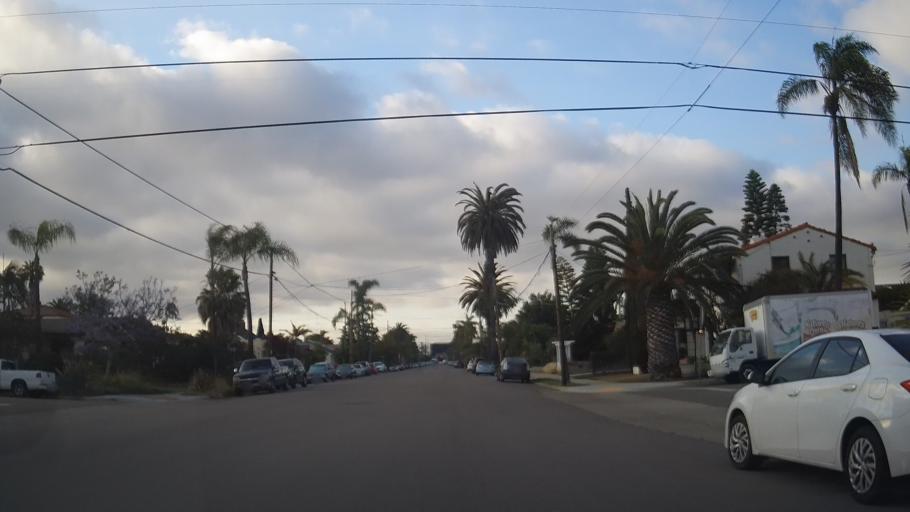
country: US
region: California
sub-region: San Diego County
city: San Diego
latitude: 32.7430
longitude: -117.1319
